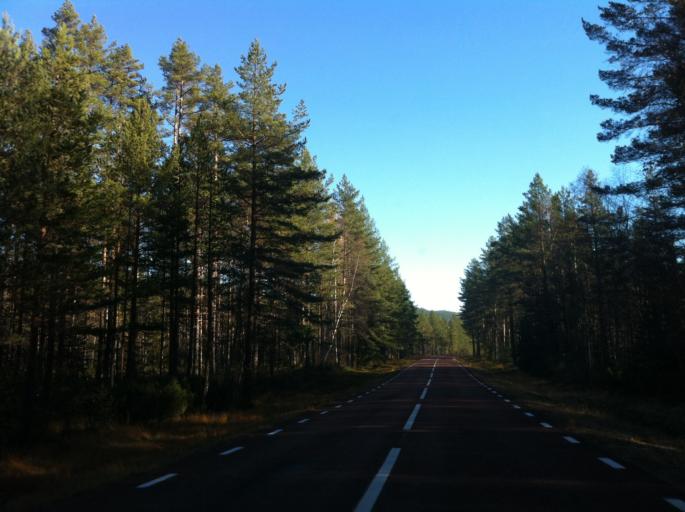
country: SE
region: Dalarna
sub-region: Alvdalens Kommun
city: AElvdalen
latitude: 61.3144
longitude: 13.6729
